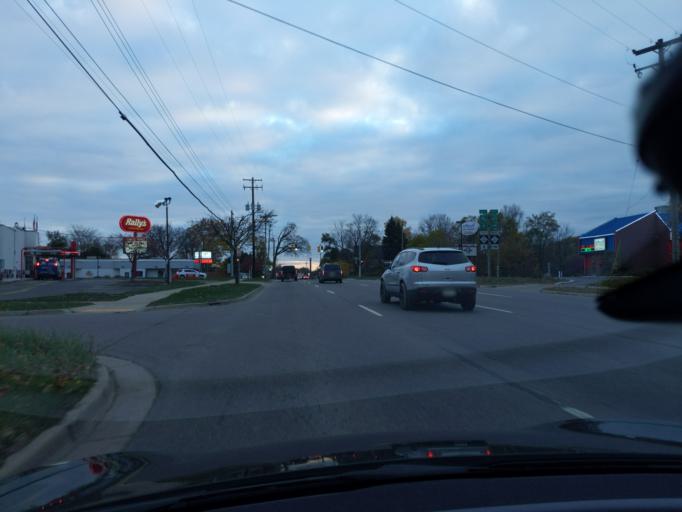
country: US
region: Michigan
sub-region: Ingham County
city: Lansing
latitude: 42.7445
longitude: -84.5465
